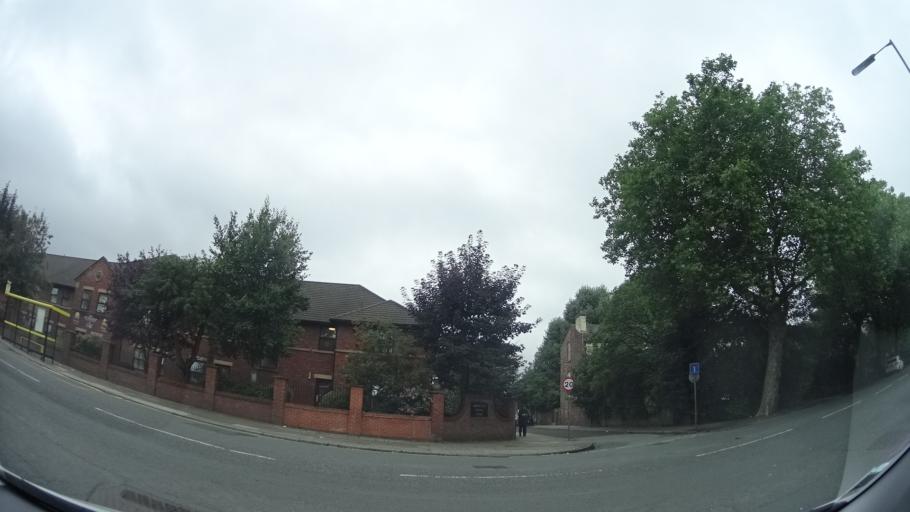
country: GB
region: England
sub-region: Liverpool
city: Liverpool
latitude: 53.4173
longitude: -2.9147
